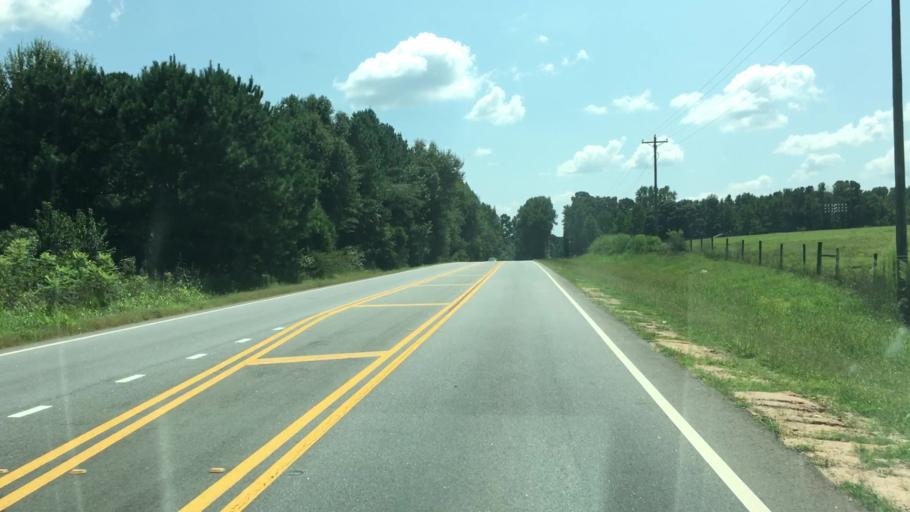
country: US
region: Georgia
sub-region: Oconee County
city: Watkinsville
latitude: 33.7764
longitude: -83.4259
